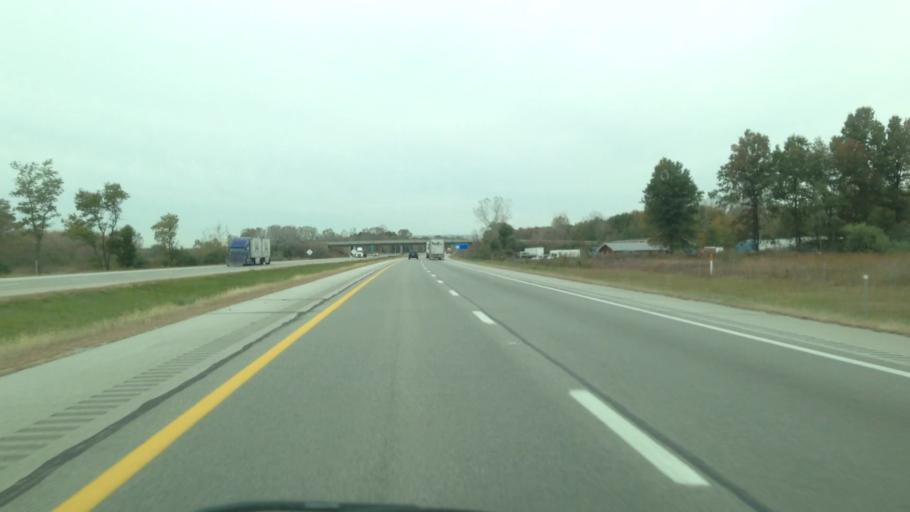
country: US
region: Ohio
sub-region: Lucas County
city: Holland
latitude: 41.5953
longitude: -83.7819
